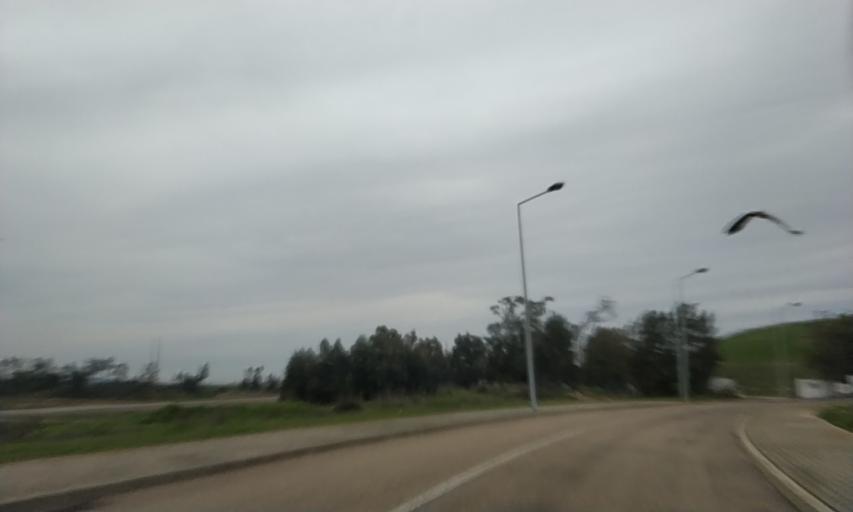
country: PT
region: Setubal
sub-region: Setubal
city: Setubal
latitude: 38.4948
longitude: -8.8187
